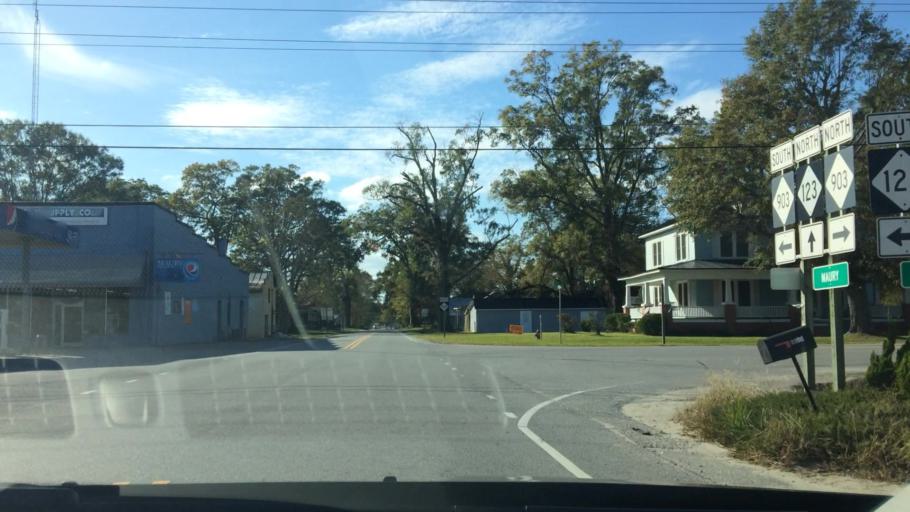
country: US
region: North Carolina
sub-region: Greene County
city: Maury
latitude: 35.4808
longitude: -77.5861
